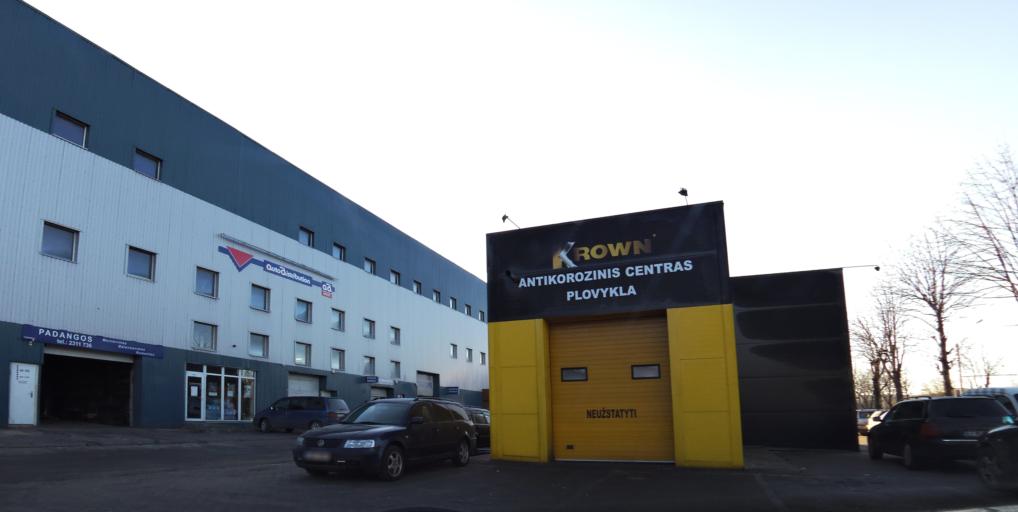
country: LT
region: Vilnius County
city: Lazdynai
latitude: 54.6553
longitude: 25.2271
